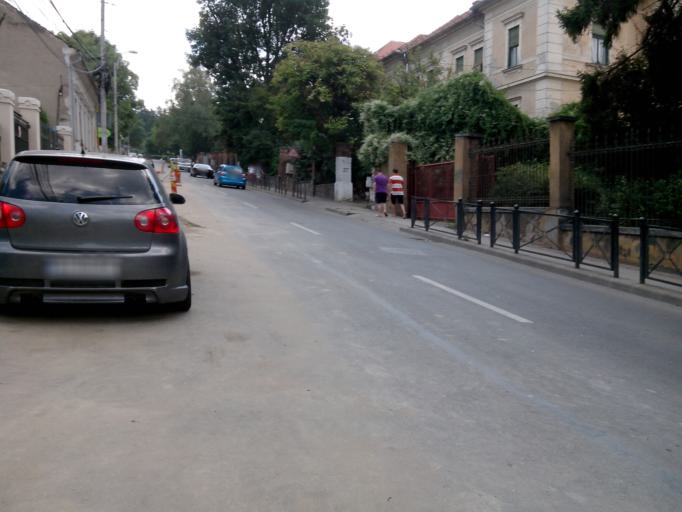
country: RO
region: Cluj
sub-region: Municipiul Cluj-Napoca
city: Cluj-Napoca
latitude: 46.7656
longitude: 23.5875
